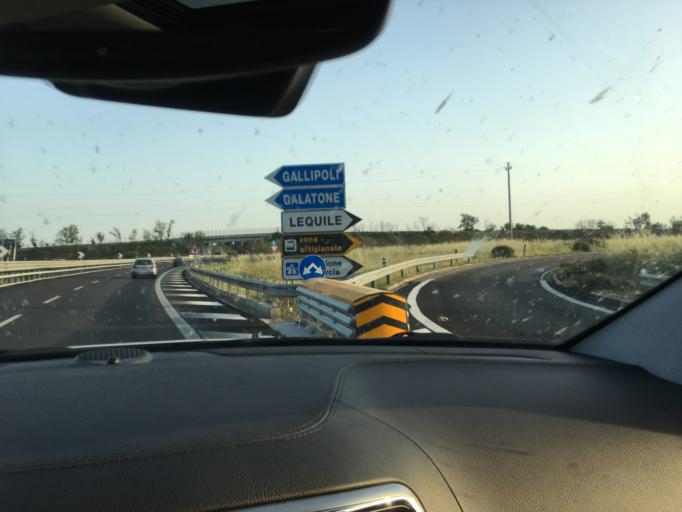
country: IT
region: Apulia
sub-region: Provincia di Lecce
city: Lequile
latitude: 40.2914
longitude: 18.1330
